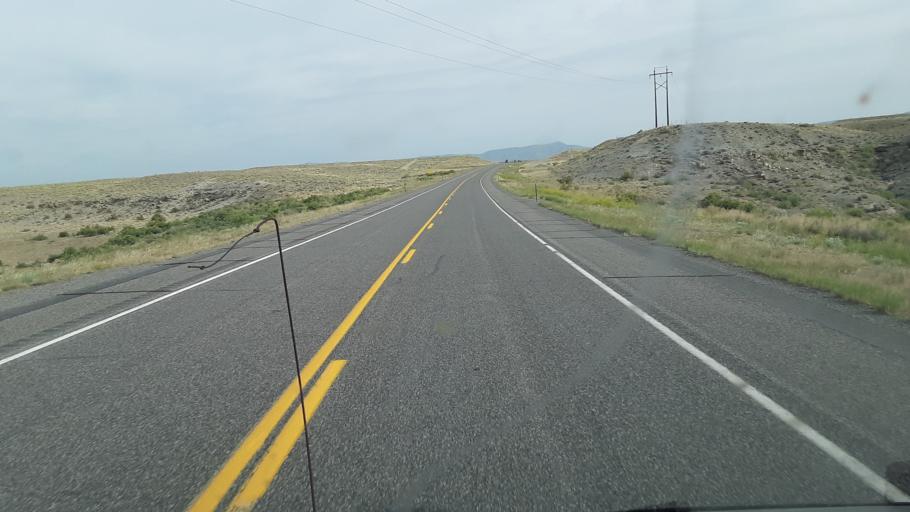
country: US
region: Wyoming
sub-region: Fremont County
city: Riverton
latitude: 43.2840
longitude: -108.1249
